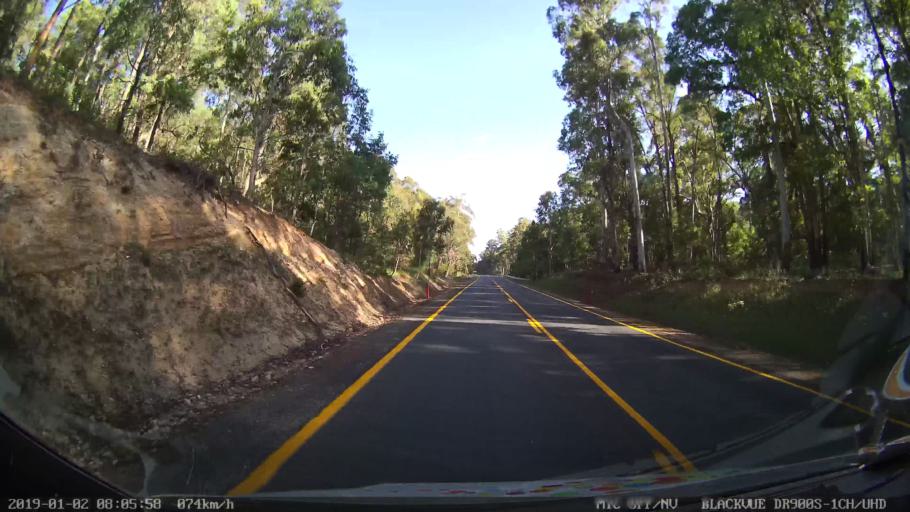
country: AU
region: New South Wales
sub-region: Tumut Shire
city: Tumut
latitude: -35.6454
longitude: 148.3872
